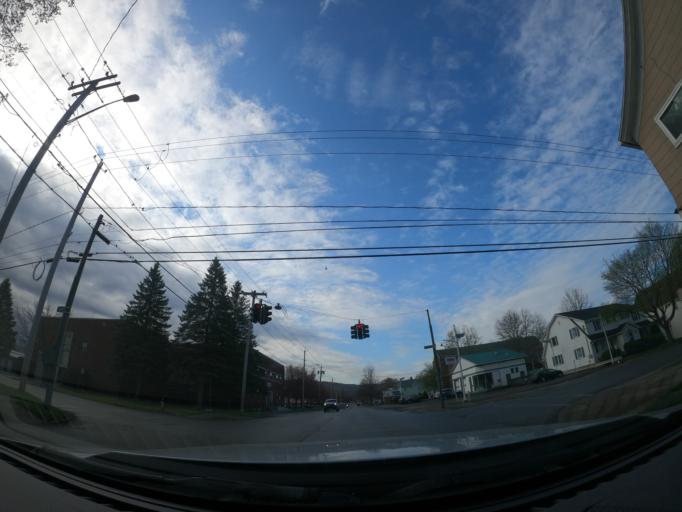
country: US
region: New York
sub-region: Cortland County
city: Cortland
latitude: 42.6024
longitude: -76.1670
